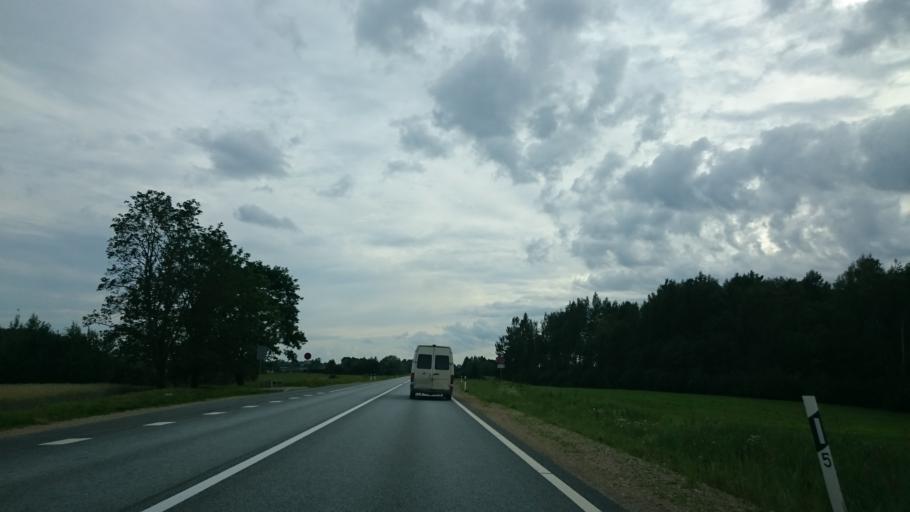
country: LV
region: Krimulda
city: Ragana
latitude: 57.1939
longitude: 24.7366
